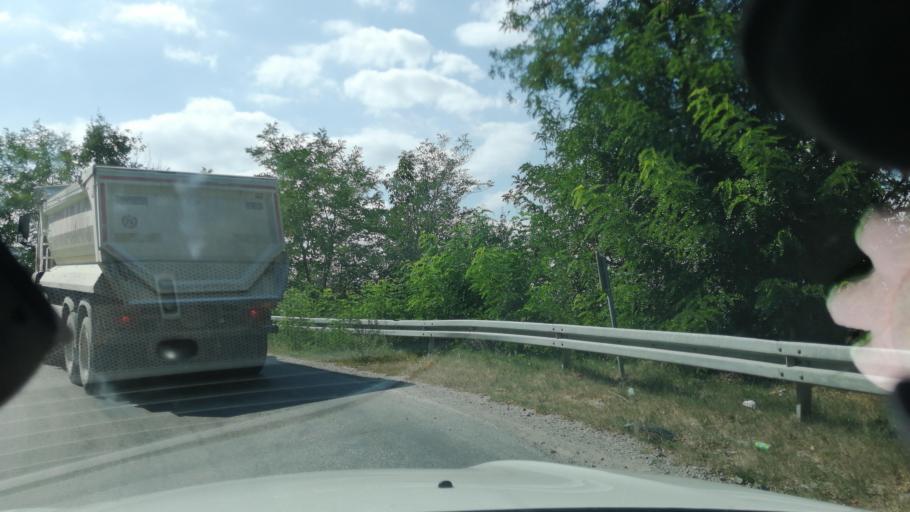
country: RS
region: Central Serbia
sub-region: Moravicki Okrug
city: Cacak
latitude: 43.8546
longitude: 20.3046
